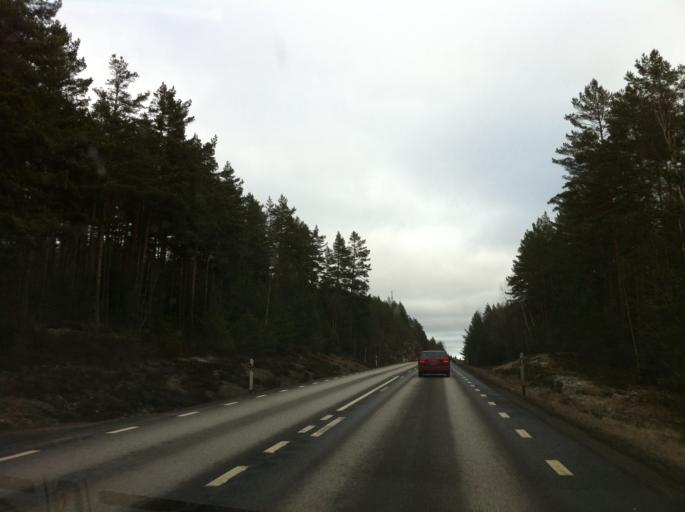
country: SE
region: Kalmar
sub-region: Vimmerby Kommun
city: Vimmerby
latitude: 57.6381
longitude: 15.7611
